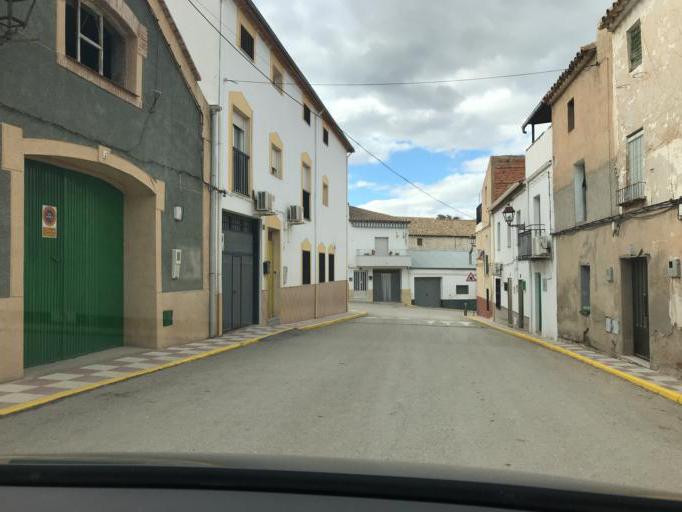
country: ES
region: Andalusia
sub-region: Provincia de Jaen
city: Jimena
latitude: 37.8734
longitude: -3.4577
